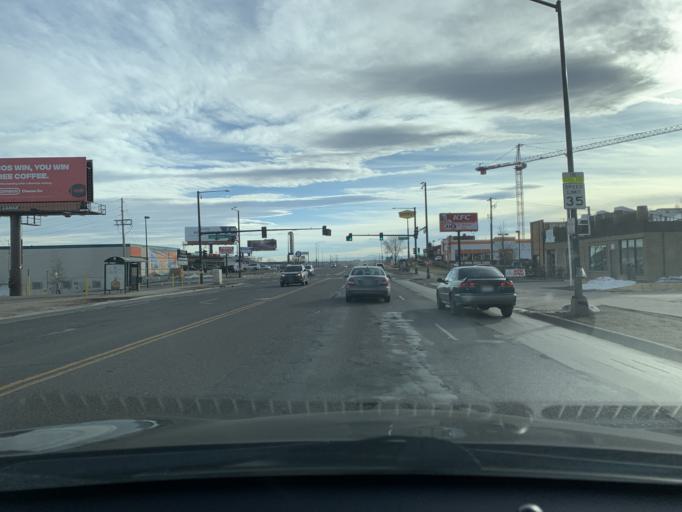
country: US
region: Colorado
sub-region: Jefferson County
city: Edgewater
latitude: 39.7446
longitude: -105.0253
